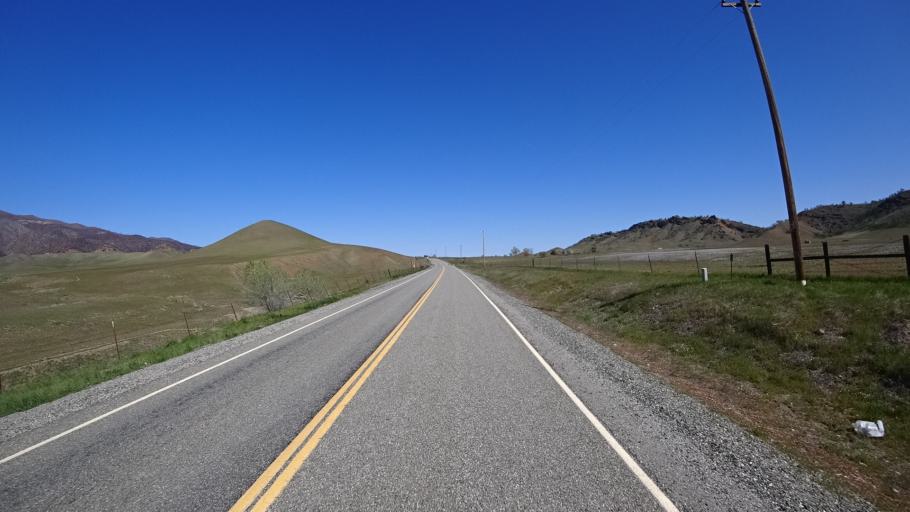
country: US
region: California
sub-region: Tehama County
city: Rancho Tehama Reserve
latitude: 39.7091
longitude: -122.5502
